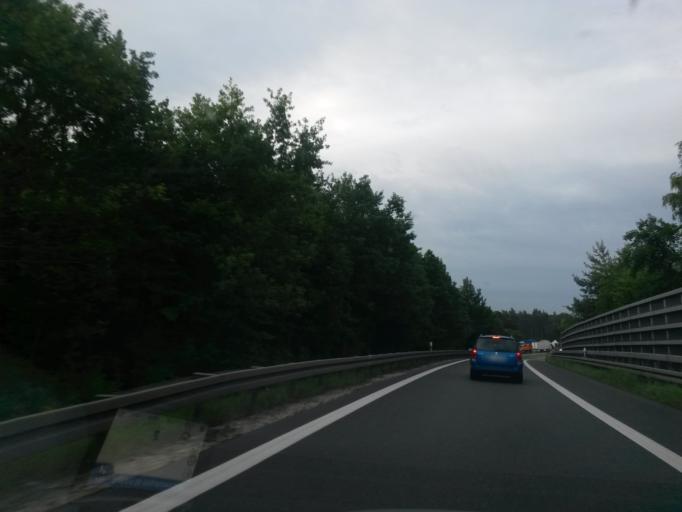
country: DE
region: Bavaria
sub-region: Regierungsbezirk Mittelfranken
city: Feucht
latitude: 49.3498
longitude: 11.2025
